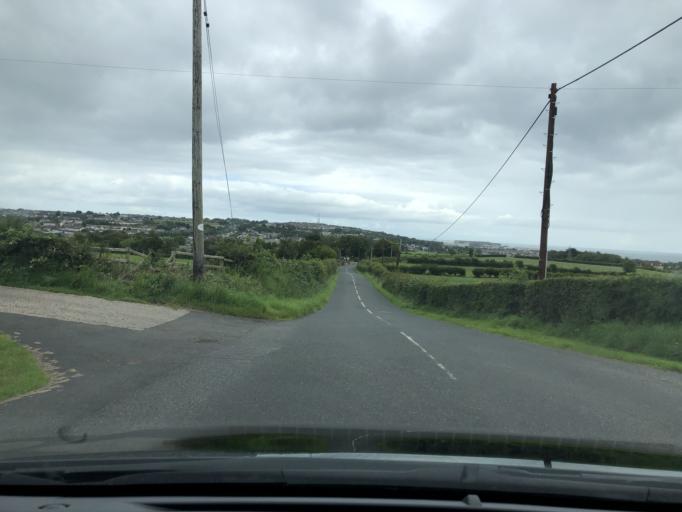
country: GB
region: Northern Ireland
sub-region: Larne District
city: Larne
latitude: 54.8412
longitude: -5.8369
